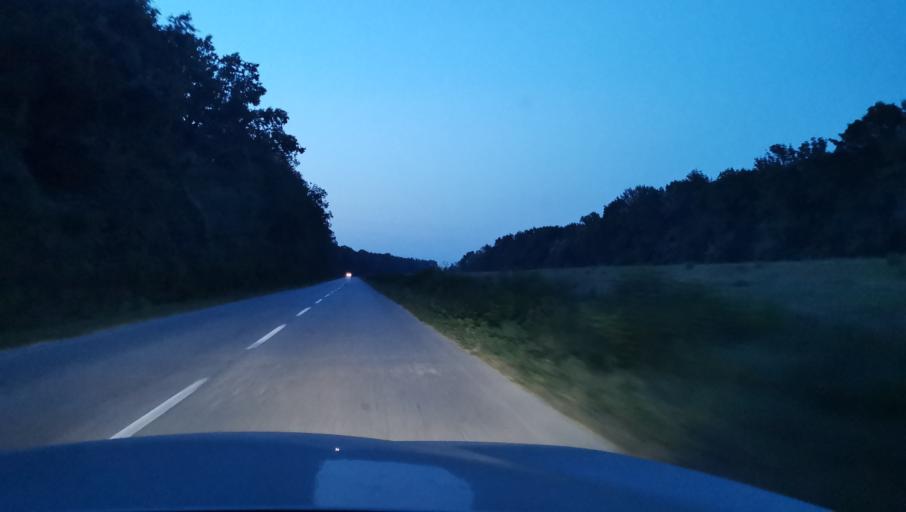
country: RS
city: Boljevci
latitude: 44.7015
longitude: 20.2026
